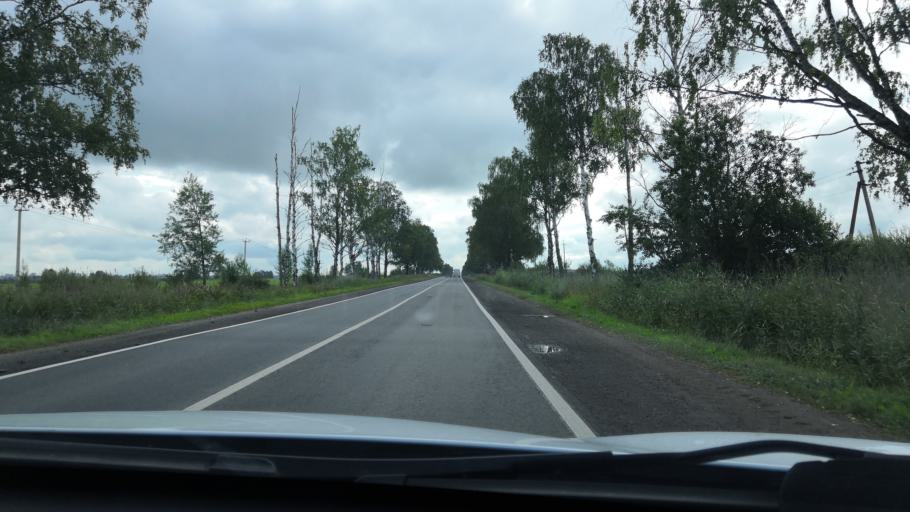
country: RU
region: St.-Petersburg
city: Tyarlevo
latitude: 59.7104
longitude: 30.4810
